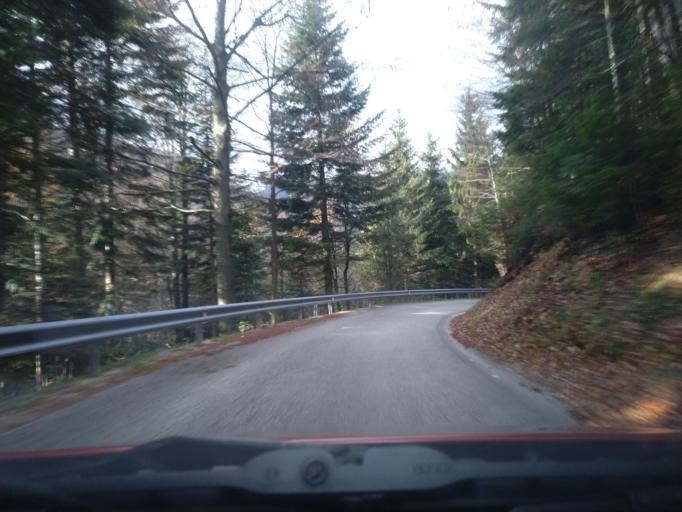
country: SI
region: Luce
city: Luce
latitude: 46.2905
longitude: 14.6971
